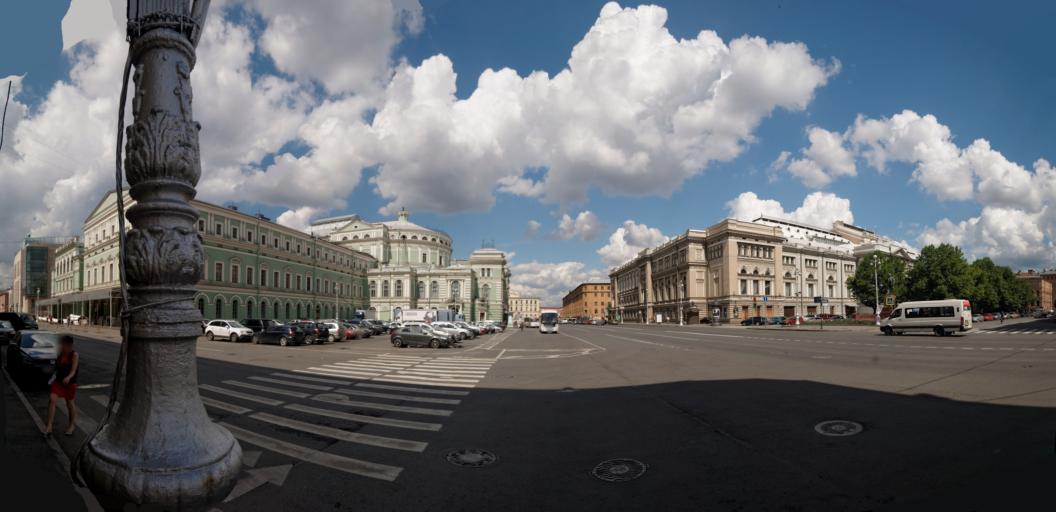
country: RU
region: St.-Petersburg
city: Saint Petersburg
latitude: 59.9247
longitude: 30.2985
